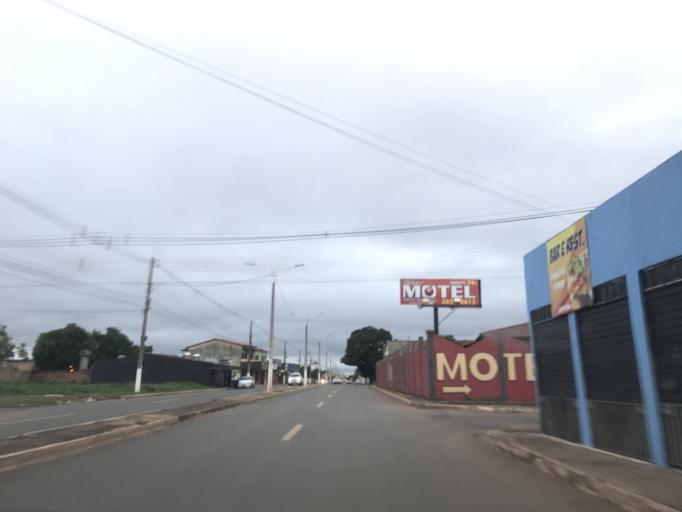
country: BR
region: Goias
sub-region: Luziania
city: Luziania
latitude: -16.2093
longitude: -47.9274
